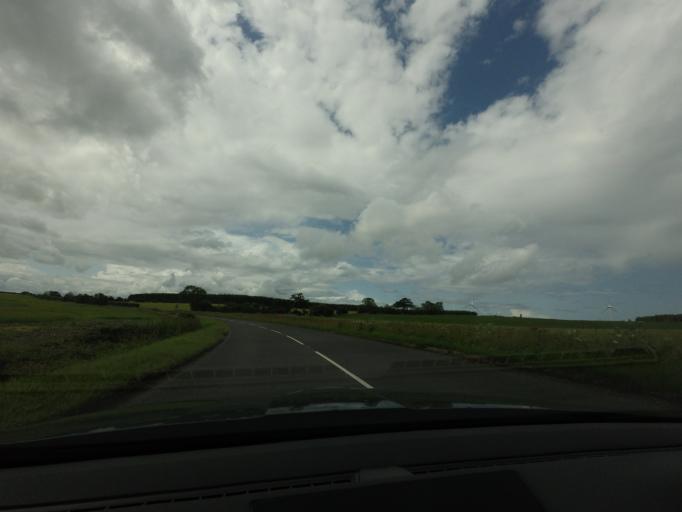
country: GB
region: Scotland
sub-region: Aberdeenshire
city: Whitehills
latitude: 57.6536
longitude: -2.6245
